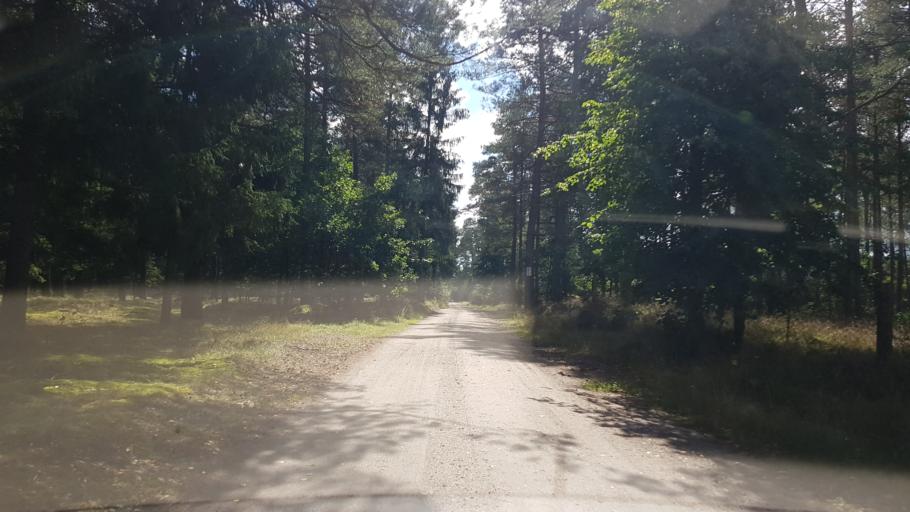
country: PL
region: West Pomeranian Voivodeship
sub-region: Powiat bialogardzki
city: Tychowo
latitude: 54.0187
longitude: 16.2990
